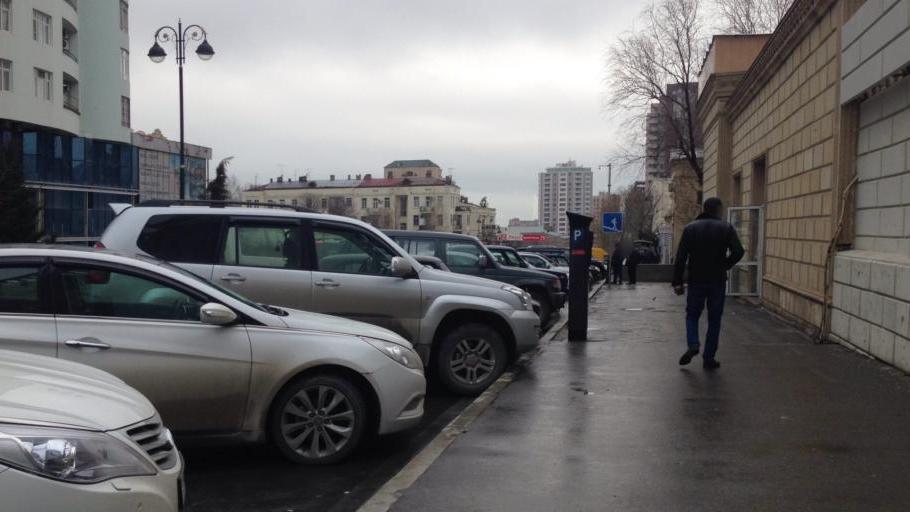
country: AZ
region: Baki
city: Baku
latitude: 40.3821
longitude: 49.8386
